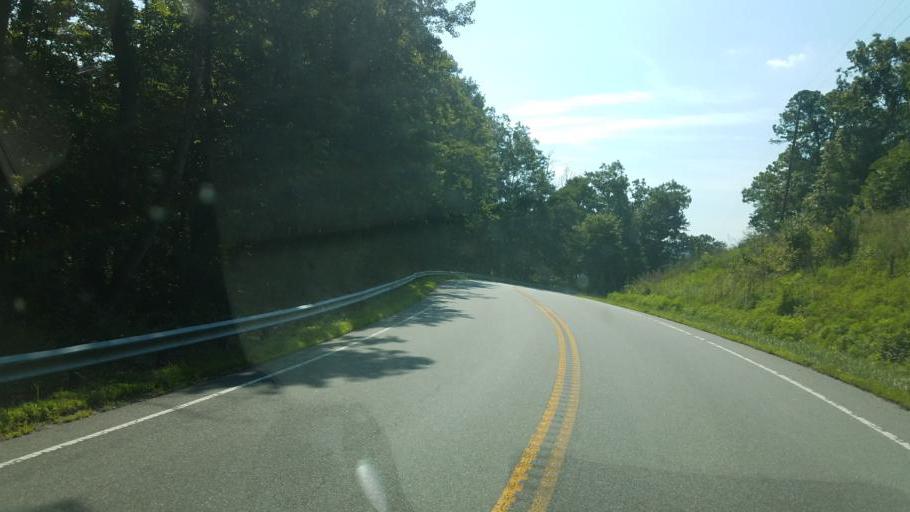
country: US
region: North Carolina
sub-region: Burke County
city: Glen Alpine
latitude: 35.9125
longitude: -81.8100
